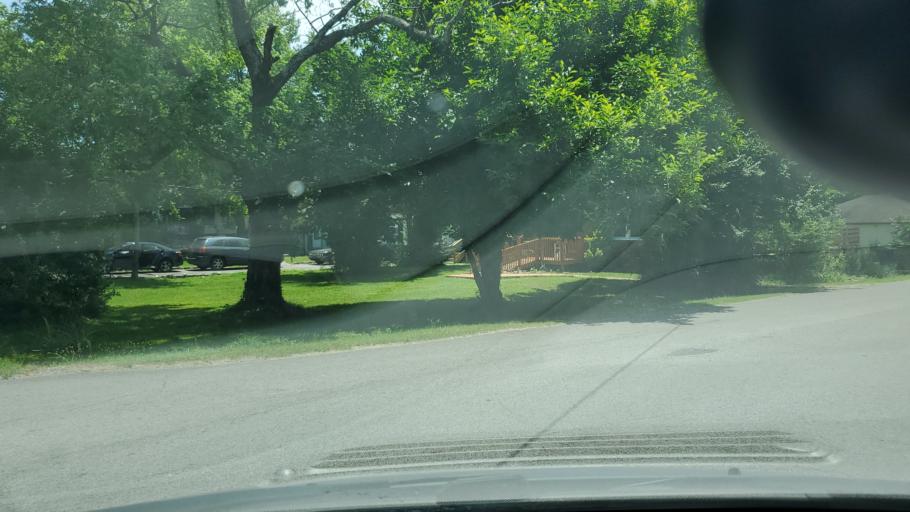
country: US
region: Tennessee
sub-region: Davidson County
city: Nashville
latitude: 36.2108
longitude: -86.7599
